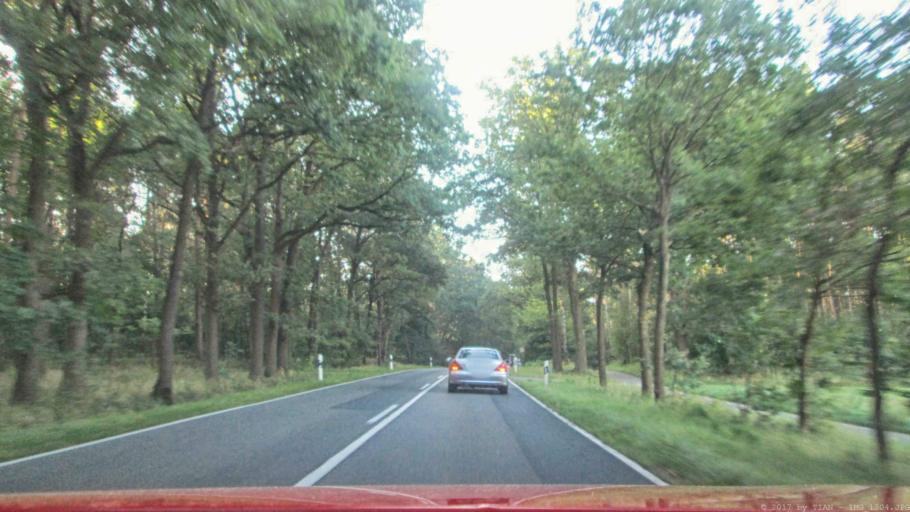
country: DE
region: Lower Saxony
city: Wieren
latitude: 52.8692
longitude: 10.6731
